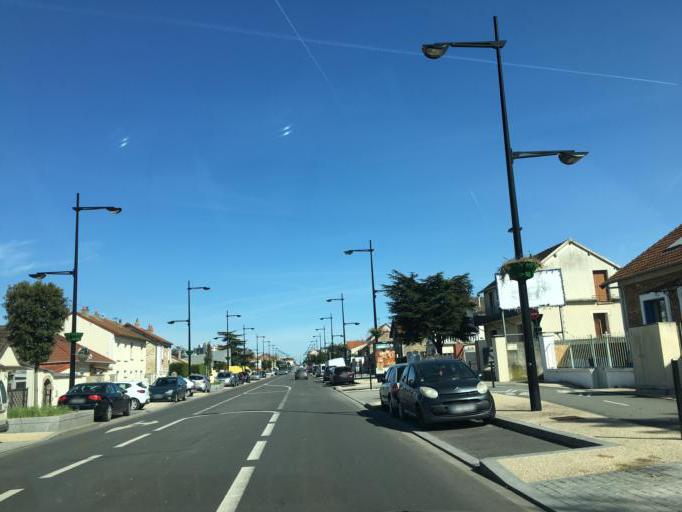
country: FR
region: Ile-de-France
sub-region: Departement de l'Essonne
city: Saintry-sur-Seine
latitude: 48.5865
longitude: 2.4769
